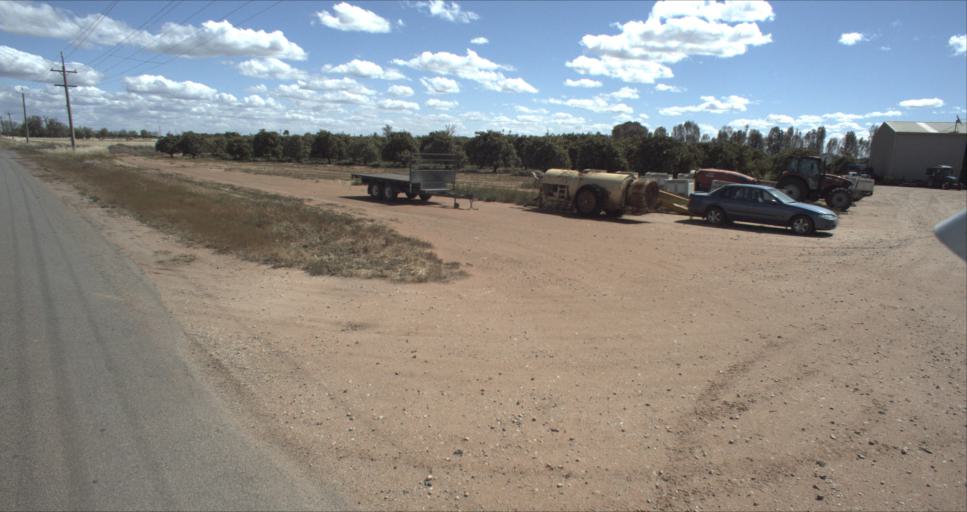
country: AU
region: New South Wales
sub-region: Leeton
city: Leeton
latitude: -34.5110
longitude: 146.2532
